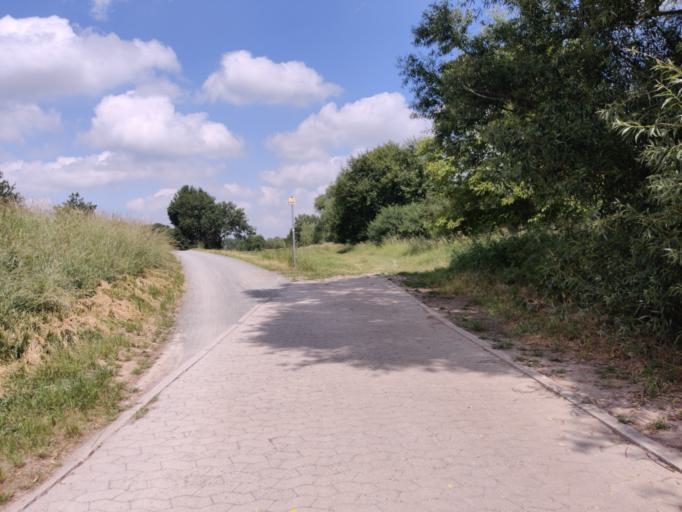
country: DE
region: Lower Saxony
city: Hildesheim
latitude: 52.1570
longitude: 9.9271
